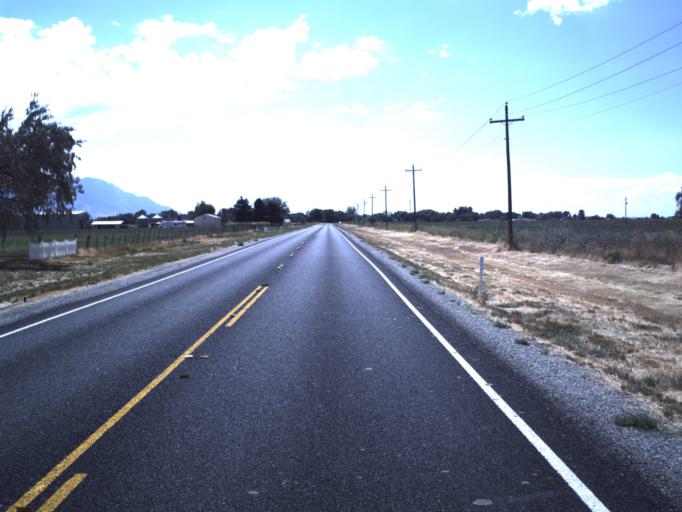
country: US
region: Utah
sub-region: Box Elder County
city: Honeyville
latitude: 41.6350
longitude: -112.1283
